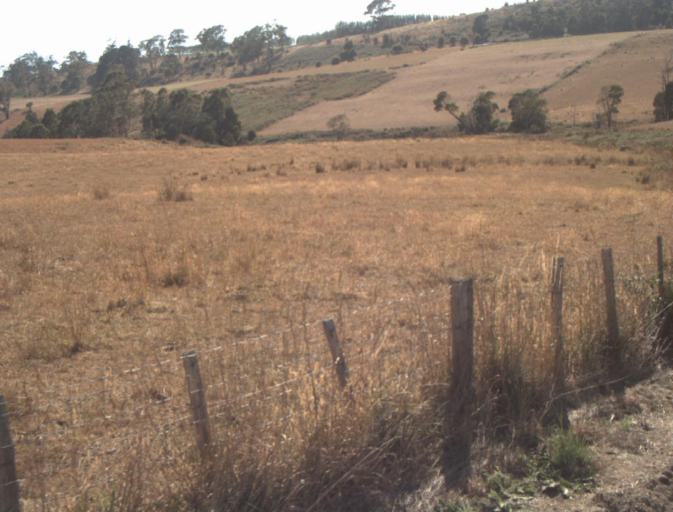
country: AU
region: Tasmania
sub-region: Launceston
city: Mayfield
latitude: -41.1695
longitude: 147.2120
